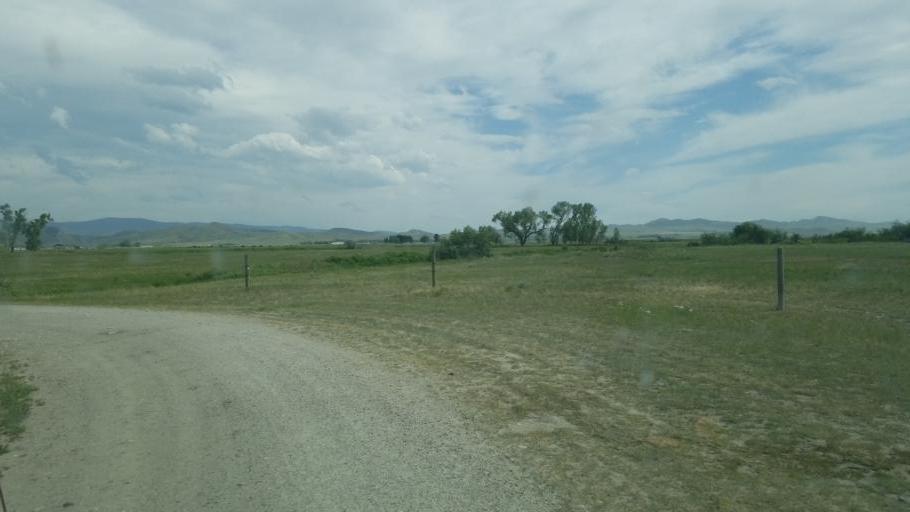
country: US
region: Montana
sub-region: Broadwater County
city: Townsend
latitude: 46.1852
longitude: -111.4807
